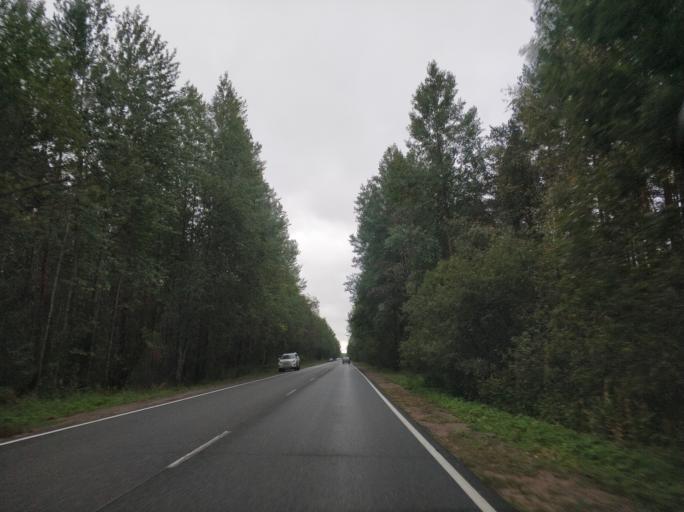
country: RU
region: Leningrad
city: Borisova Griva
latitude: 60.1504
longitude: 30.9377
